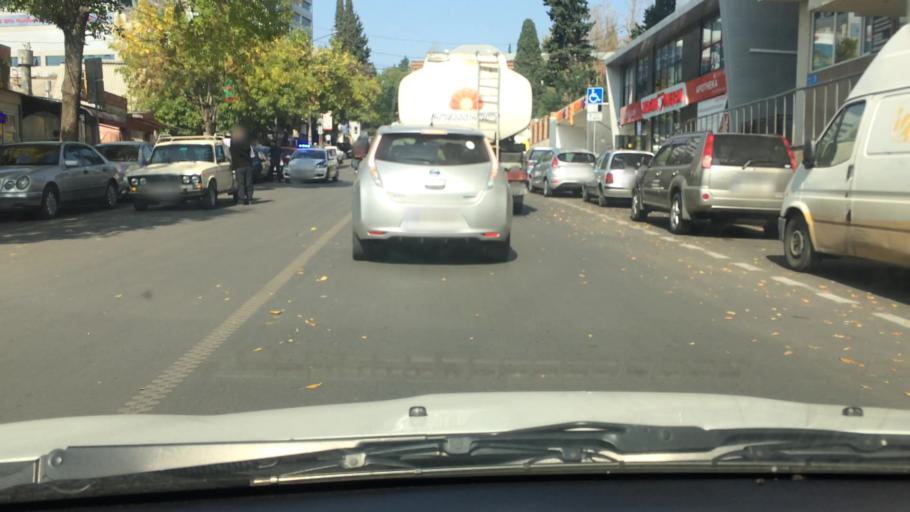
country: GE
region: T'bilisi
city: Tbilisi
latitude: 41.6898
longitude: 44.8278
